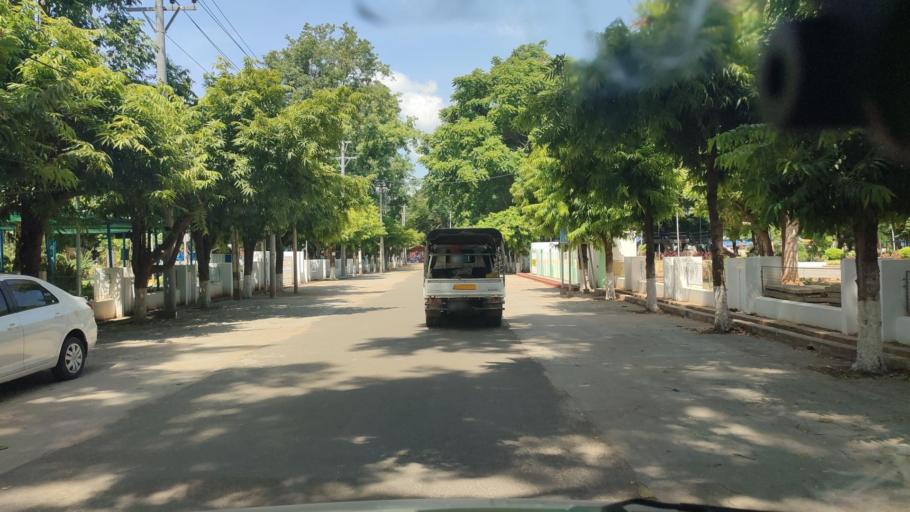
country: MM
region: Magway
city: Magway
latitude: 20.1441
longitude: 94.9244
